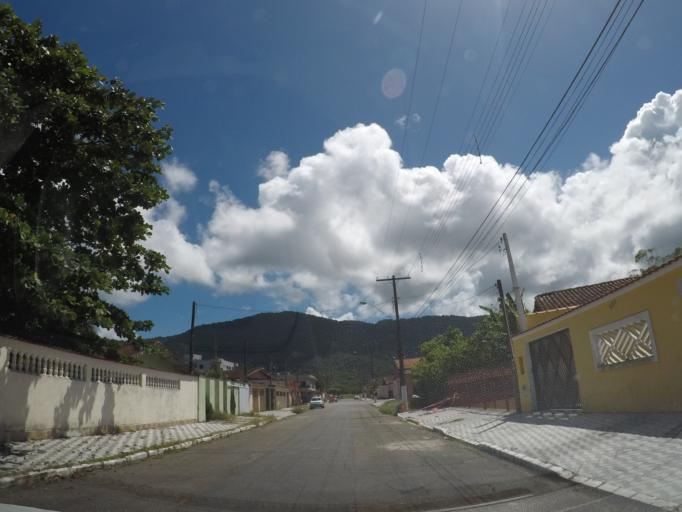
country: BR
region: Sao Paulo
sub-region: Mongagua
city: Mongagua
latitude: -24.0752
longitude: -46.5826
